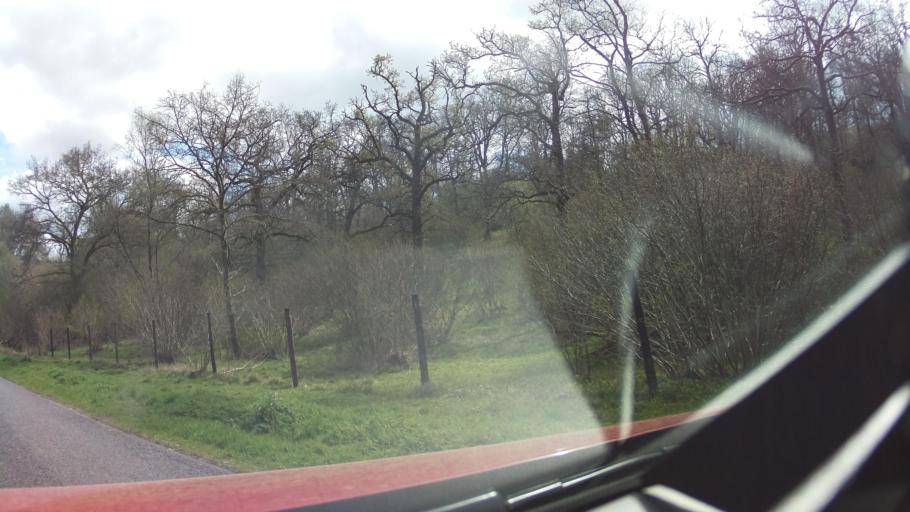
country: GB
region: England
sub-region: Hampshire
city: Highclere
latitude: 51.3005
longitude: -1.4500
